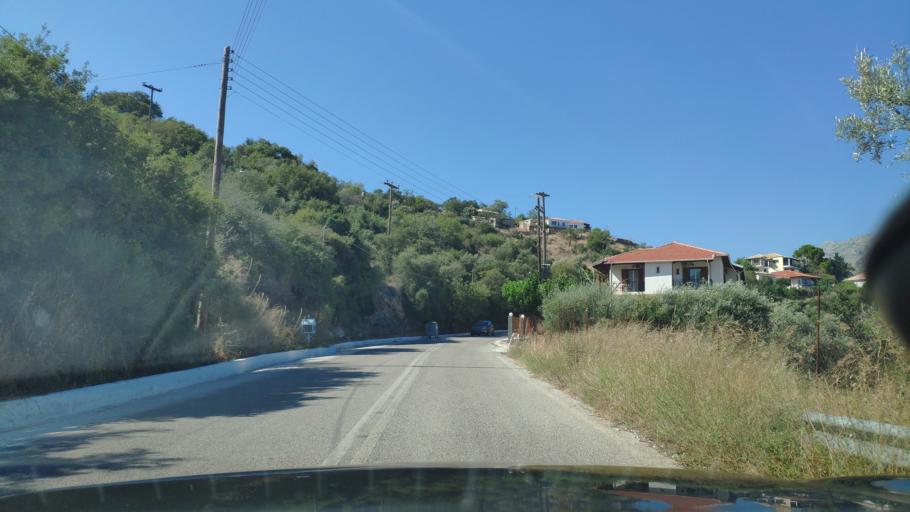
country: GR
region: Ionian Islands
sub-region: Lefkada
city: Nidri
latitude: 38.6609
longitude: 20.6000
